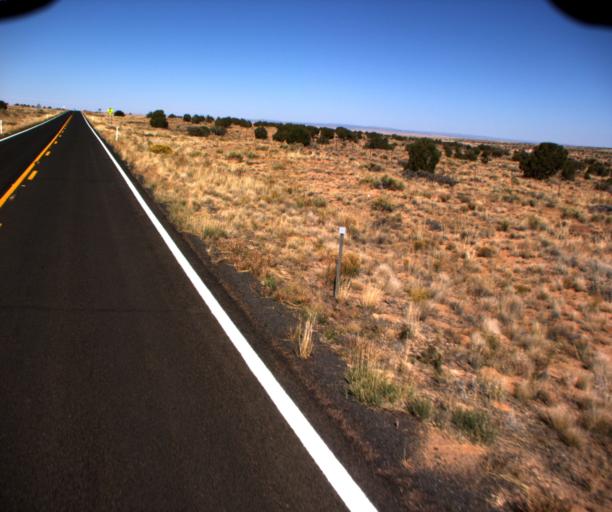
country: US
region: Arizona
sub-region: Coconino County
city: Tuba City
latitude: 35.9097
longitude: -110.8843
